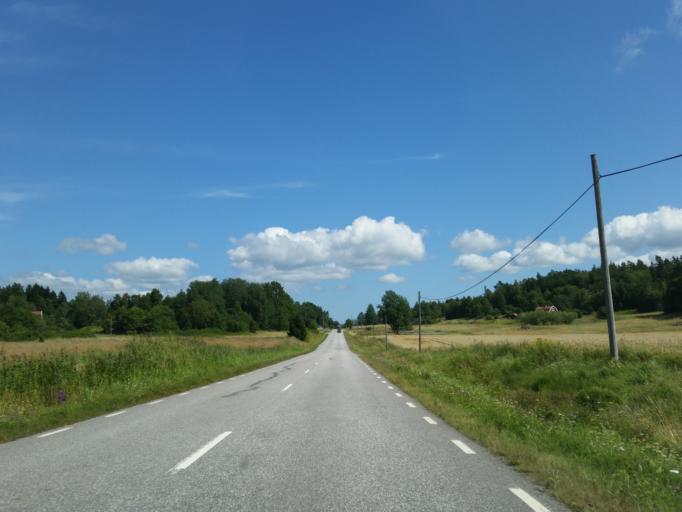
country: SE
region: Soedermanland
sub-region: Trosa Kommun
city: Trosa
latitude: 58.9920
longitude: 17.6633
